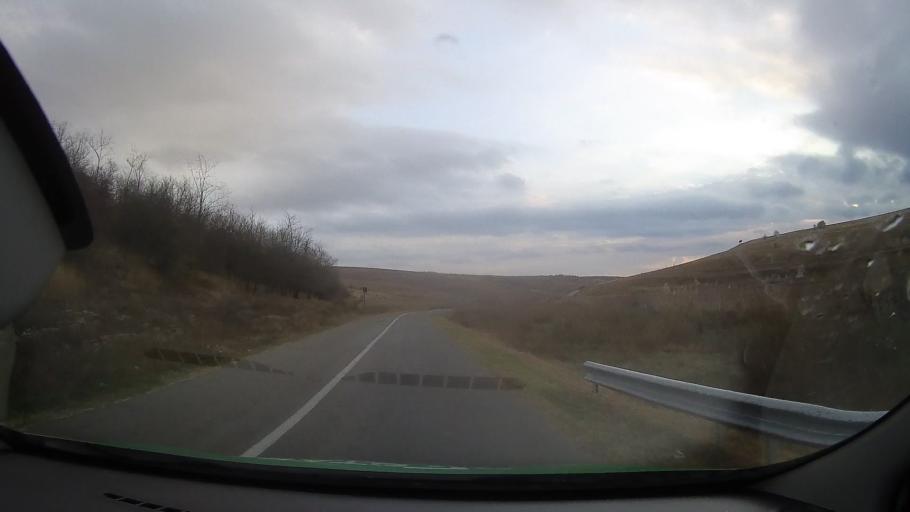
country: RO
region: Constanta
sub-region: Comuna Dobromir
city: Dobromir
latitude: 44.0359
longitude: 27.8024
